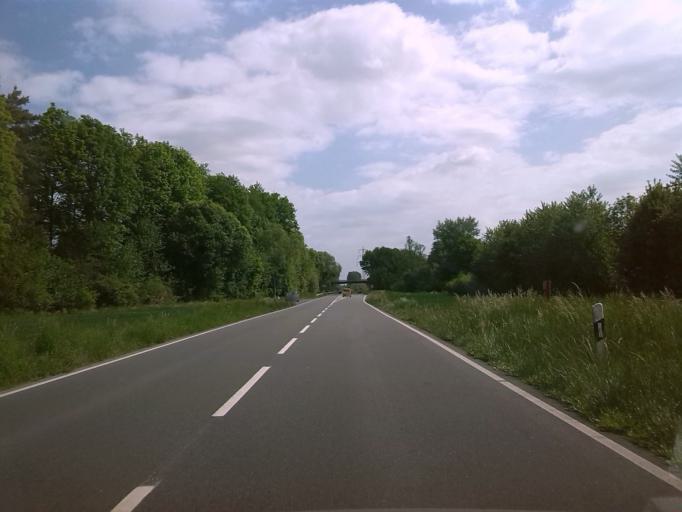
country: DE
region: Hesse
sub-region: Regierungsbezirk Darmstadt
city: Gross-Zimmern
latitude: 49.8819
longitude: 8.8096
